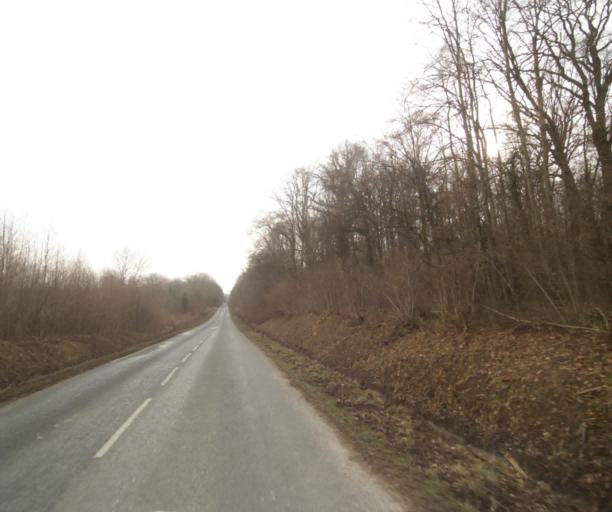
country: FR
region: Champagne-Ardenne
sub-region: Departement de la Haute-Marne
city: Villiers-en-Lieu
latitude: 48.7148
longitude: 4.8831
